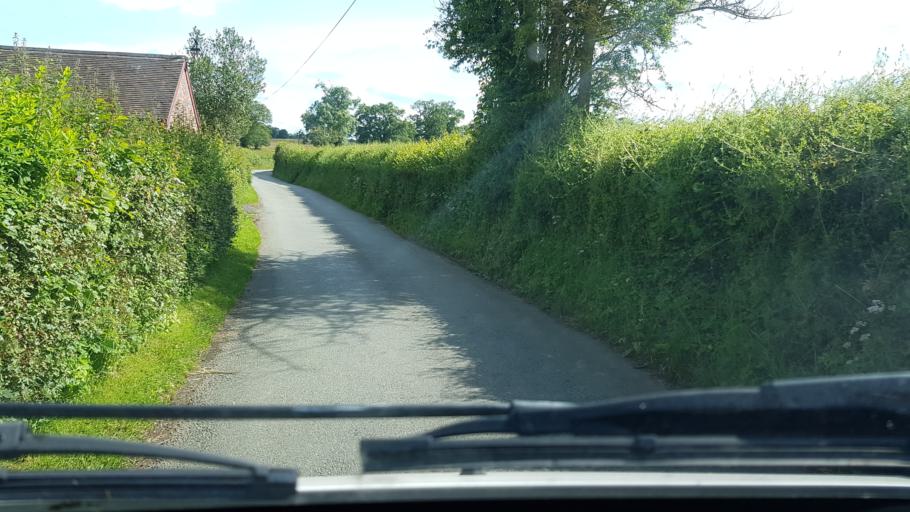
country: GB
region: England
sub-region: Shropshire
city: Romsley
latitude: 52.4406
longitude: -2.3037
